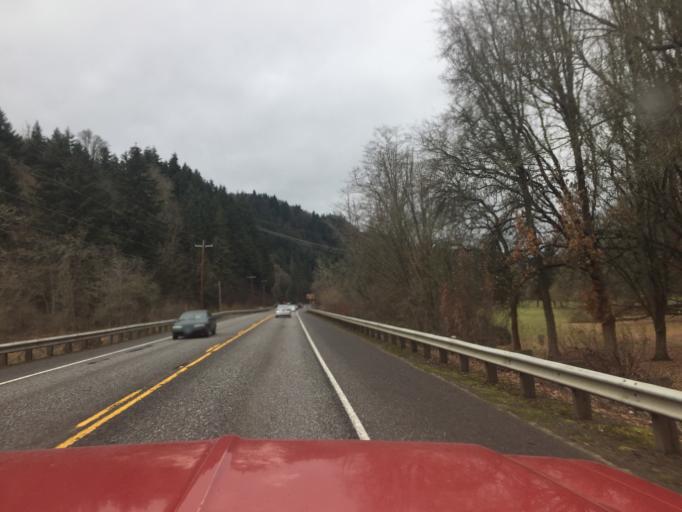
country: US
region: Washington
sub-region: Cowlitz County
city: Kalama
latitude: 46.0332
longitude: -122.8913
